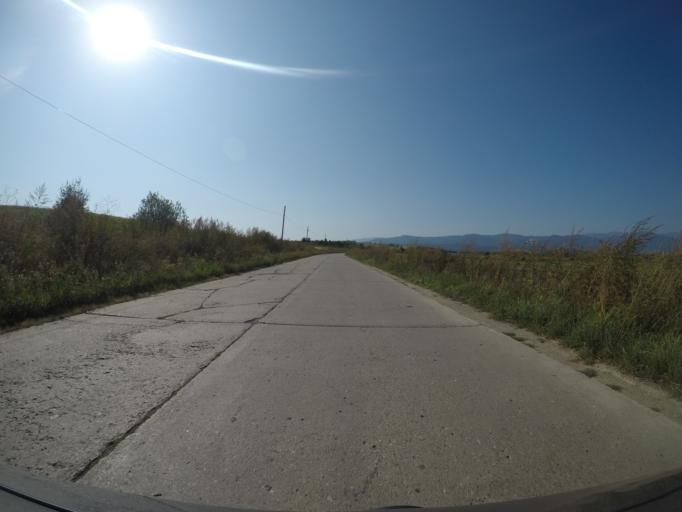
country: RO
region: Brasov
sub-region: Comuna Sinca Veche
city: Persani
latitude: 45.7843
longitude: 25.1915
